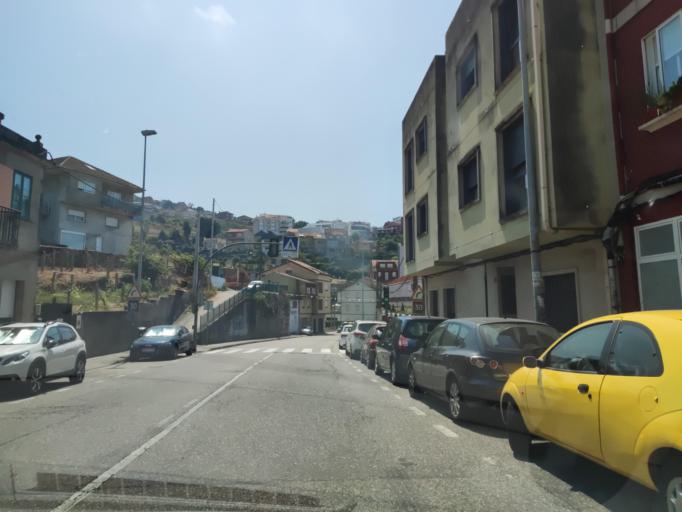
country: ES
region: Galicia
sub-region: Provincia de Pontevedra
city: Redondela
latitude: 42.2715
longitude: -8.6664
